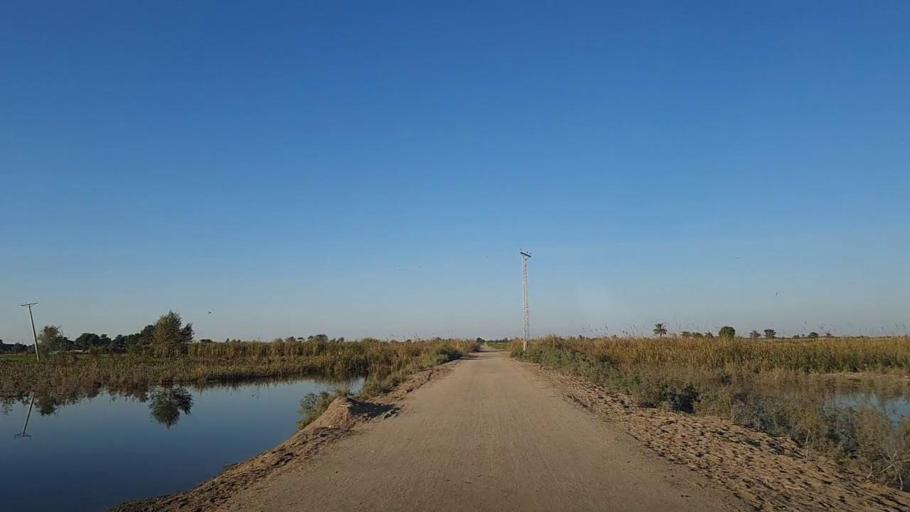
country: PK
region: Sindh
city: Sanghar
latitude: 26.1413
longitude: 68.9265
